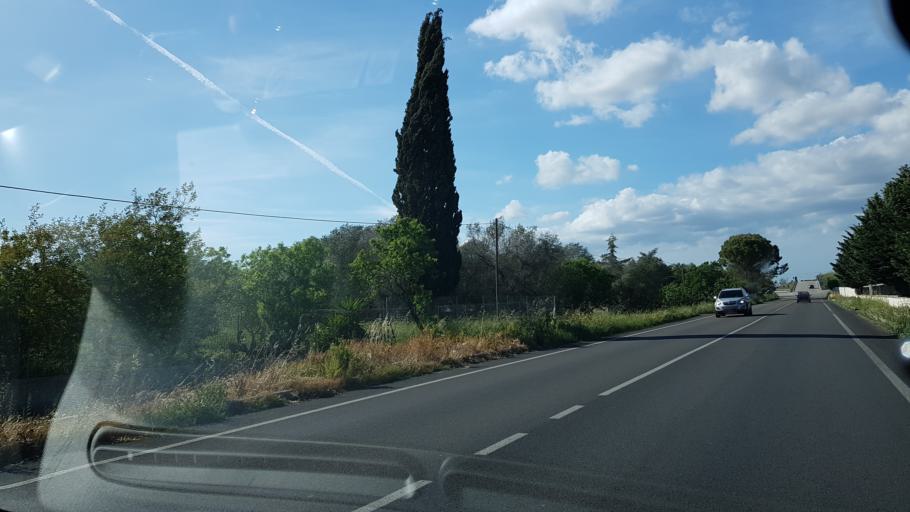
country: IT
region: Apulia
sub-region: Provincia di Brindisi
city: Mesagne
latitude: 40.5639
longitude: 17.7871
